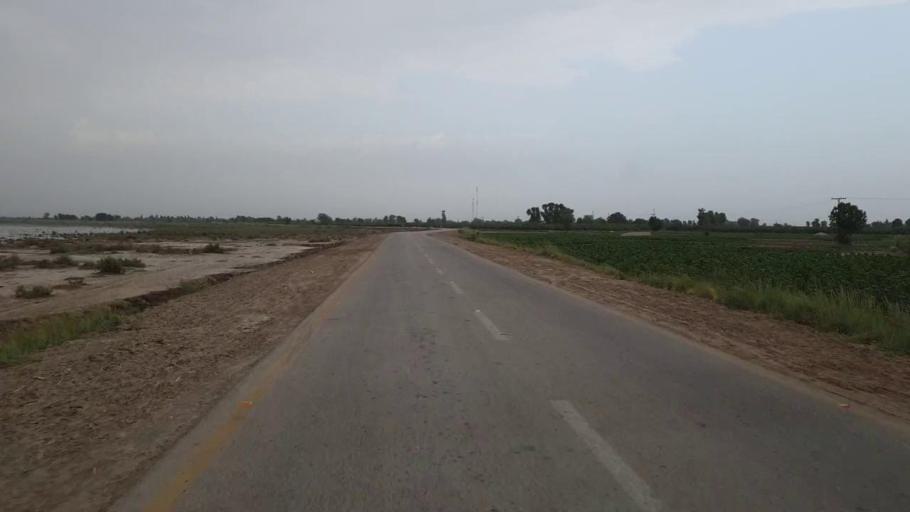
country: PK
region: Sindh
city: Bandhi
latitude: 26.5795
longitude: 68.2782
